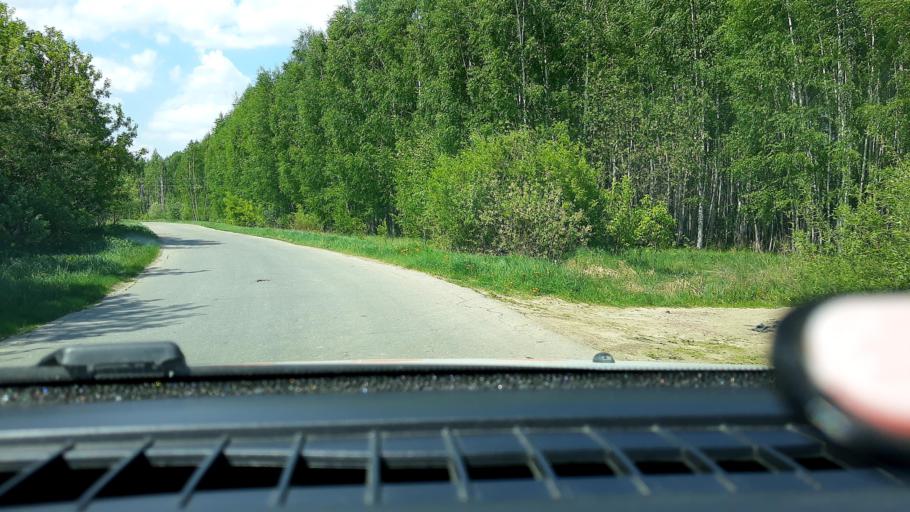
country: RU
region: Nizjnij Novgorod
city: Kstovo
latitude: 56.1473
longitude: 44.1300
